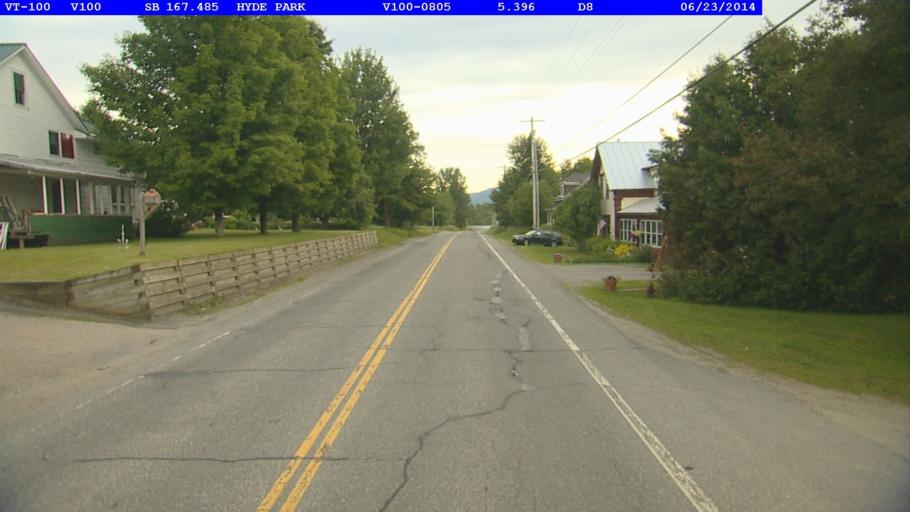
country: US
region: Vermont
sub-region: Lamoille County
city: Hyde Park
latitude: 44.6693
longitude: -72.6009
